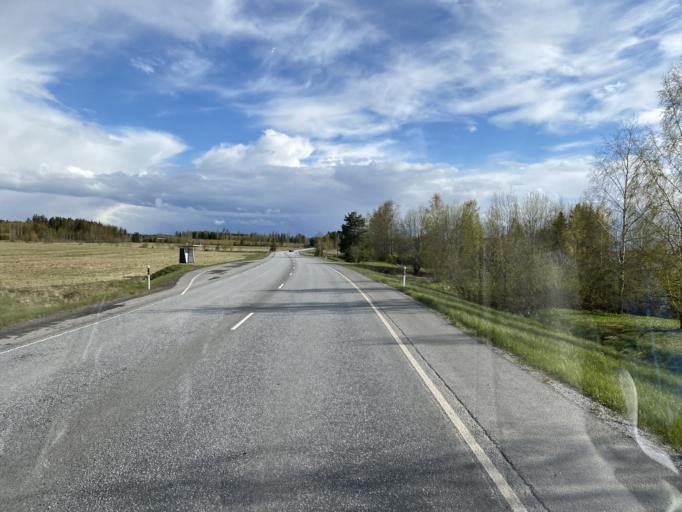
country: FI
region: Pirkanmaa
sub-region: Tampere
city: Lempaeaelae
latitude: 61.2919
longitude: 23.7421
